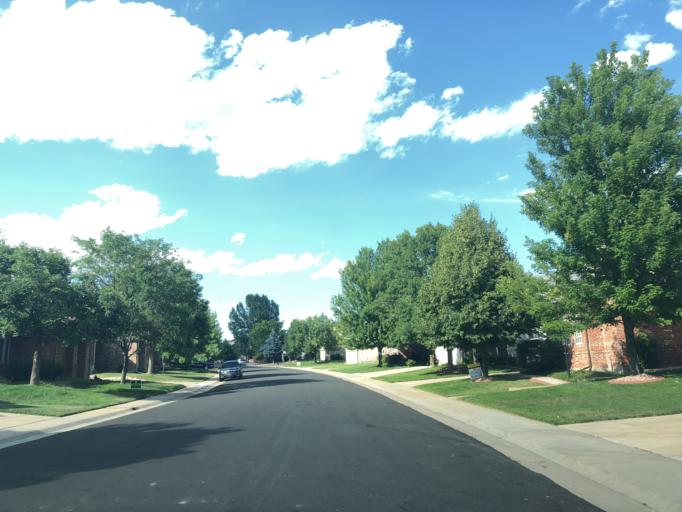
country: US
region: Colorado
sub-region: Arapahoe County
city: Dove Valley
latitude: 39.6092
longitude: -104.7622
